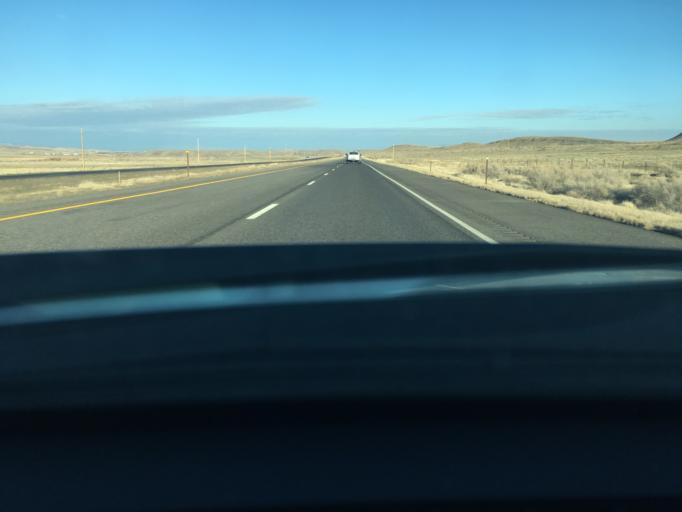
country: US
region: Colorado
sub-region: Mesa County
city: Clifton
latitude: 38.9007
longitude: -108.3670
